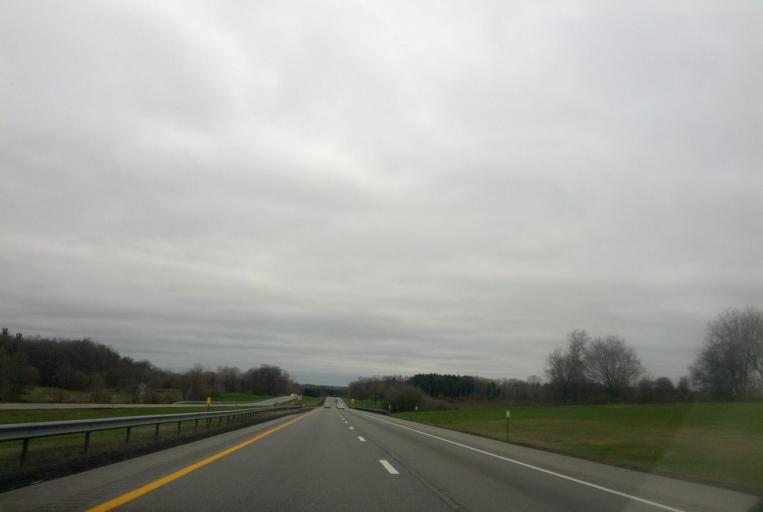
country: US
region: New York
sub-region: Ontario County
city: Phelps
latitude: 42.9555
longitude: -77.0090
